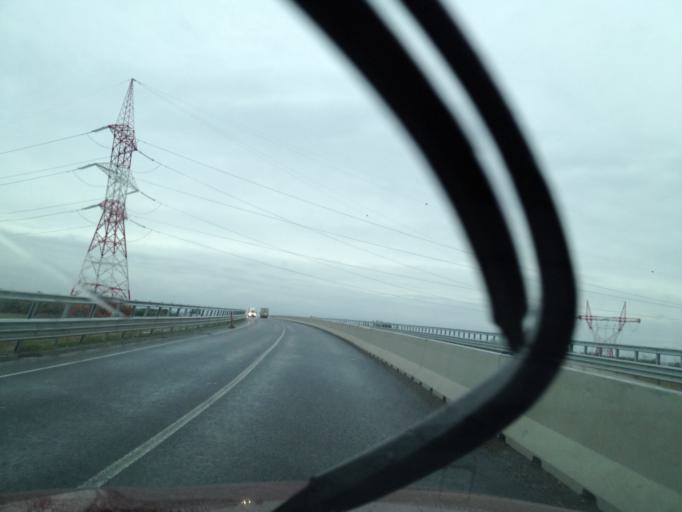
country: RO
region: Brasov
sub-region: Comuna Sanpetru
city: Sanpetru
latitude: 45.6886
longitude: 25.6515
